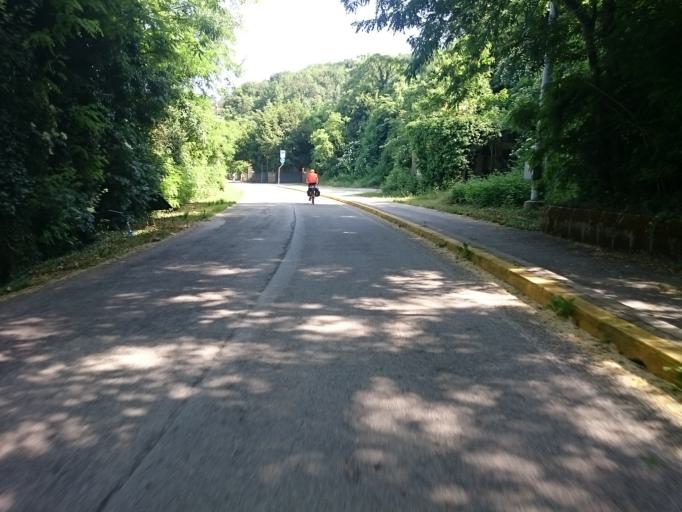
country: IT
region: Veneto
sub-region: Provincia di Padova
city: Bastia
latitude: 45.3772
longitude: 11.6716
